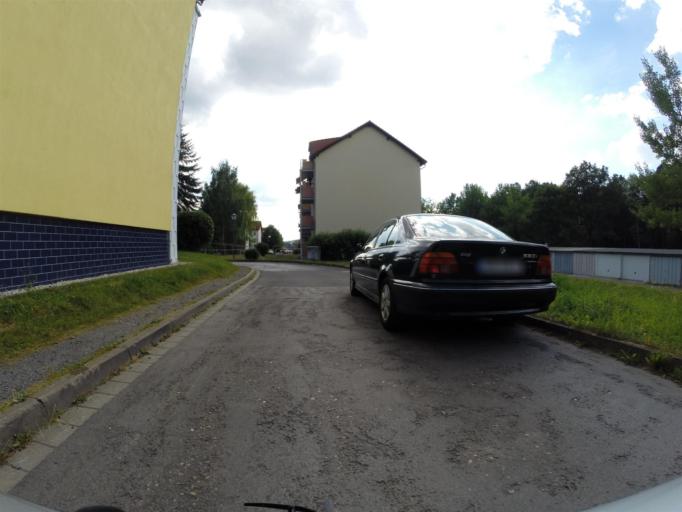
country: DE
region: Thuringia
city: Stadtroda
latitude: 50.8654
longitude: 11.7388
